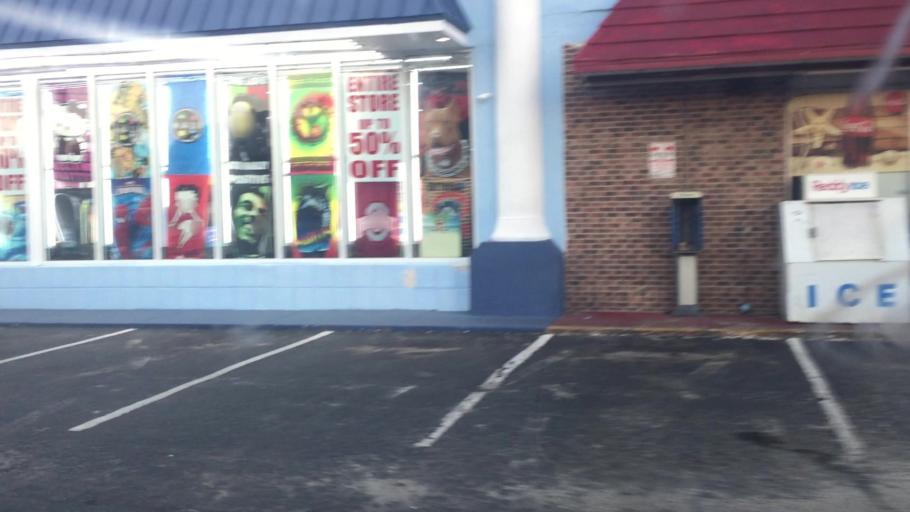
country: US
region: South Carolina
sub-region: Horry County
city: Myrtle Beach
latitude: 33.6800
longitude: -78.8977
